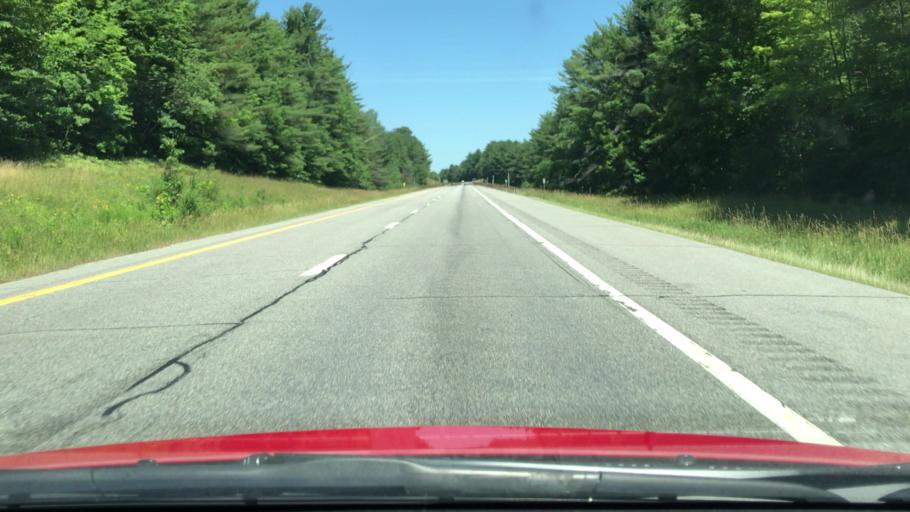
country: US
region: New York
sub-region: Essex County
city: Elizabethtown
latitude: 44.1457
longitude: -73.5835
